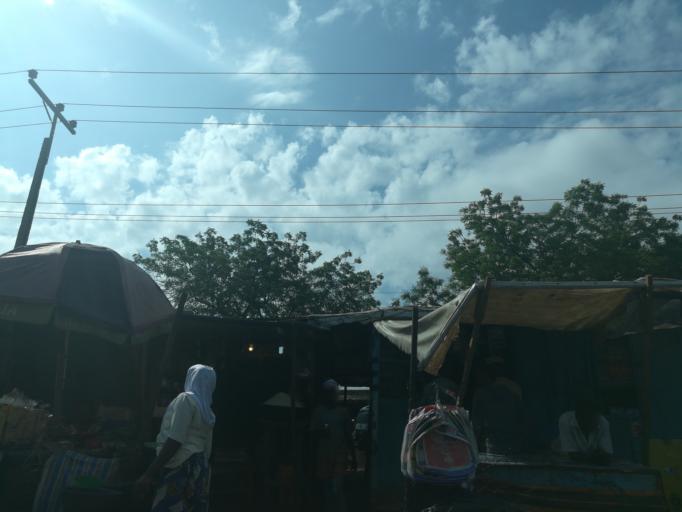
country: NG
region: Lagos
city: Ikorodu
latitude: 6.6270
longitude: 3.5075
